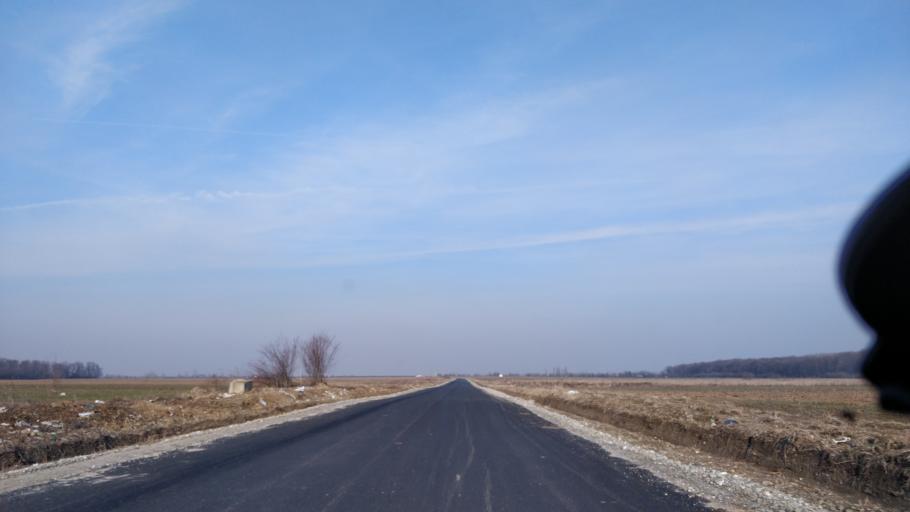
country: RO
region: Dambovita
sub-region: Comuna Brezoaiele
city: Brezoaia
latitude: 44.5274
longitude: 25.7854
